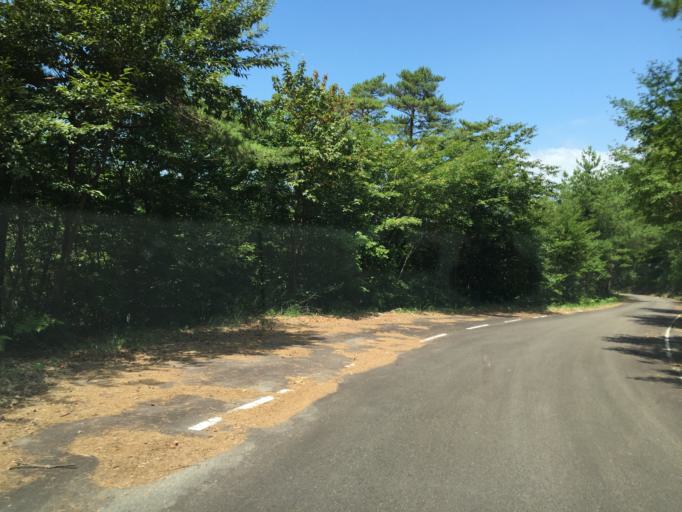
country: JP
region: Fukushima
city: Inawashiro
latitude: 37.4440
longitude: 140.0596
